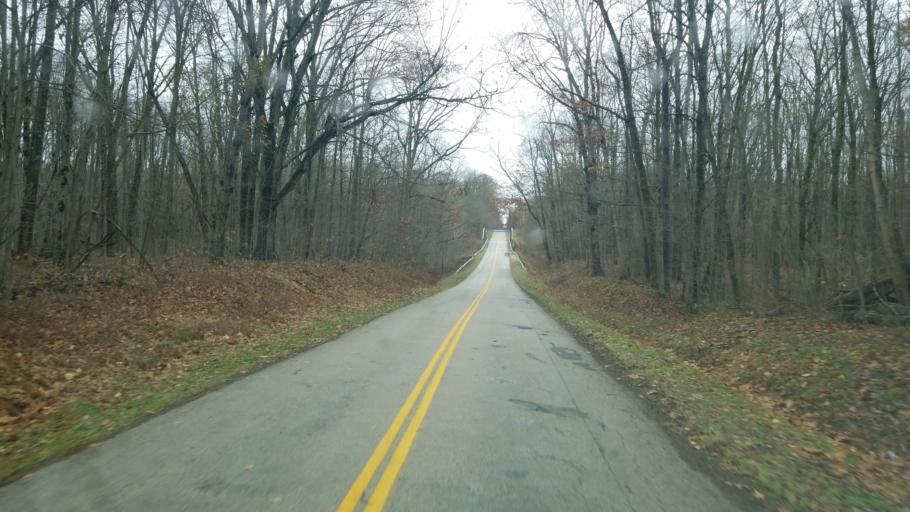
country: US
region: Ohio
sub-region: Ashtabula County
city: Roaming Shores
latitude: 41.7098
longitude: -80.8723
